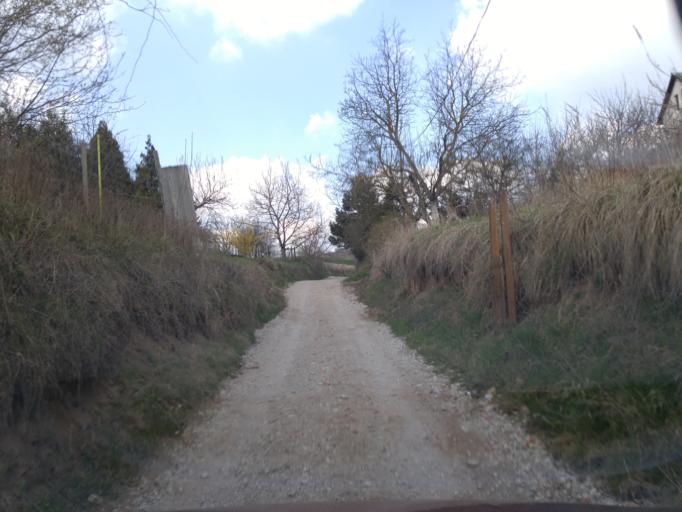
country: HU
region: Somogy
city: Adand
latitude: 46.8062
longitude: 18.1028
